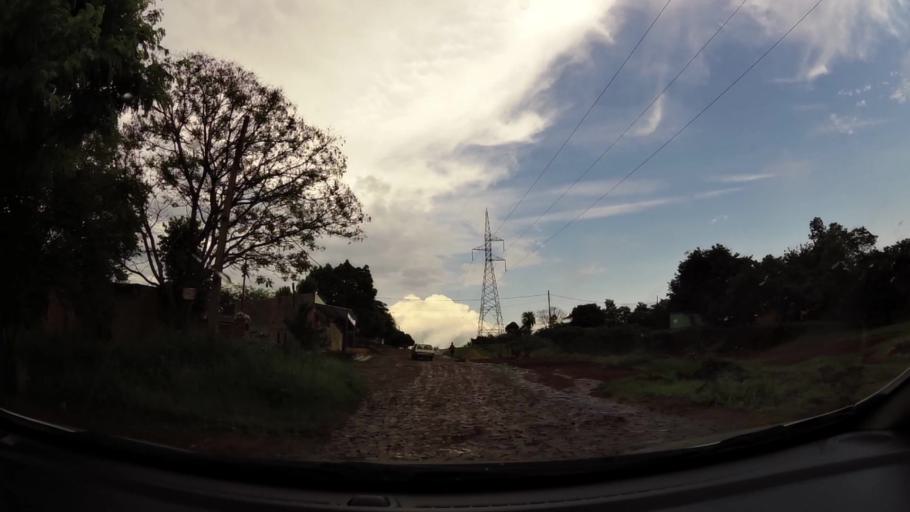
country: PY
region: Alto Parana
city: Presidente Franco
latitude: -25.5341
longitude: -54.6653
